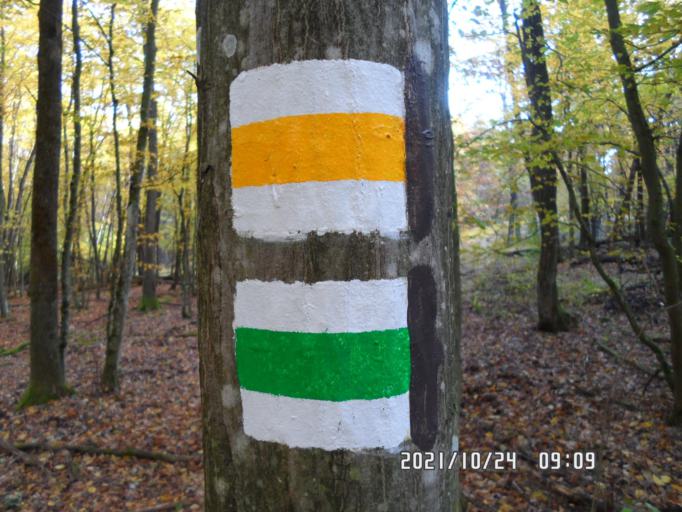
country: SI
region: Hodos-Hodos
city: Hodos
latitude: 46.8432
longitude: 16.3392
